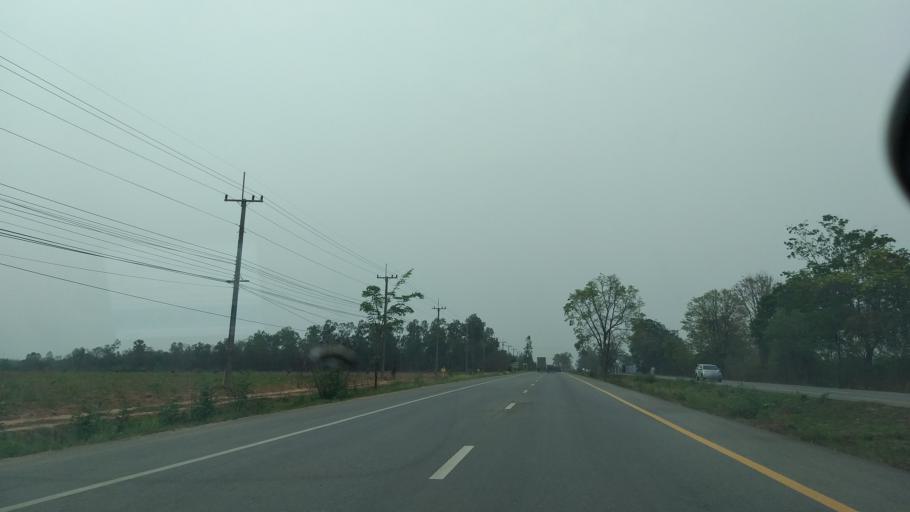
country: TH
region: Chachoengsao
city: Plaeng Yao
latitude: 13.5055
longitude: 101.2700
